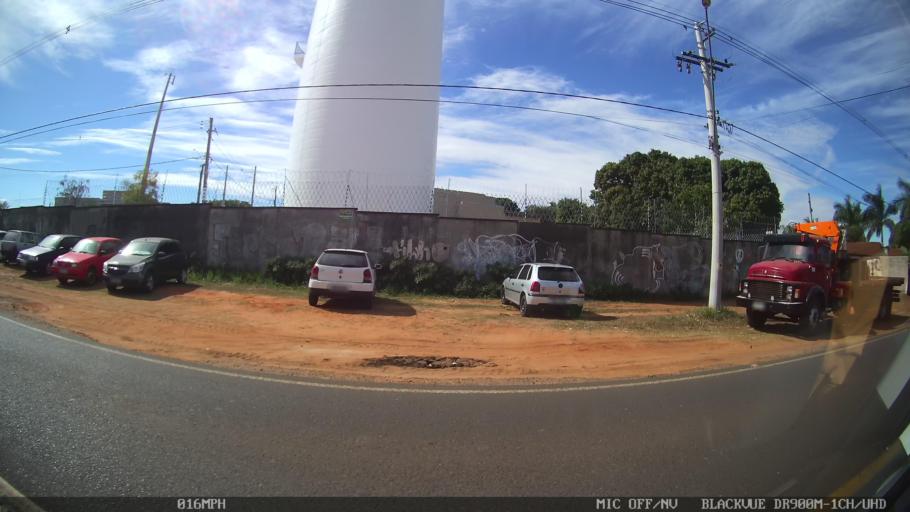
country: BR
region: Sao Paulo
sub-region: Sao Jose Do Rio Preto
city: Sao Jose do Rio Preto
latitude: -20.8357
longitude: -49.3370
